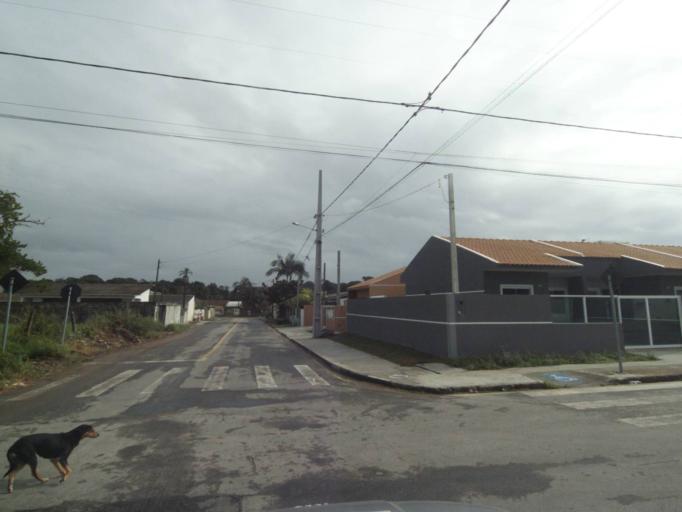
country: BR
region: Parana
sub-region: Paranagua
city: Paranagua
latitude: -25.5662
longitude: -48.5727
